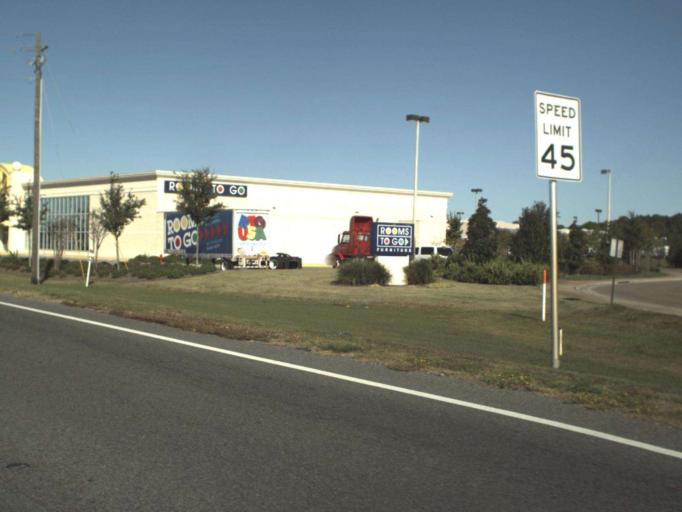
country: US
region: Florida
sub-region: Walton County
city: Miramar Beach
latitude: 30.3894
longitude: -86.4178
